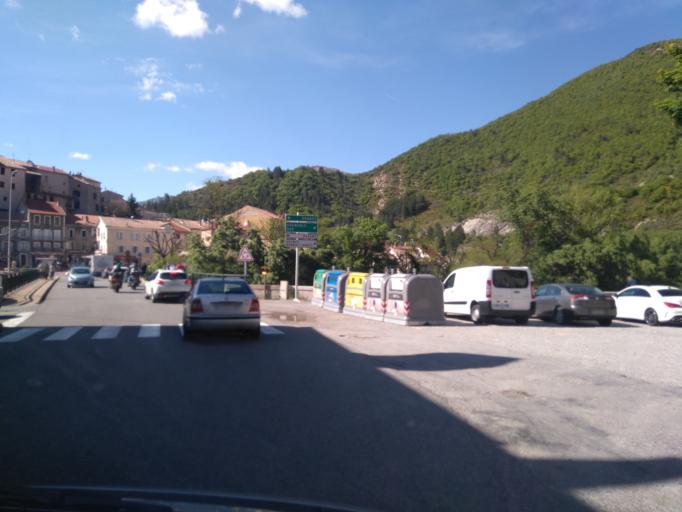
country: FR
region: Provence-Alpes-Cote d'Azur
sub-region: Departement des Hautes-Alpes
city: Serres
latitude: 44.4285
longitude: 5.7180
